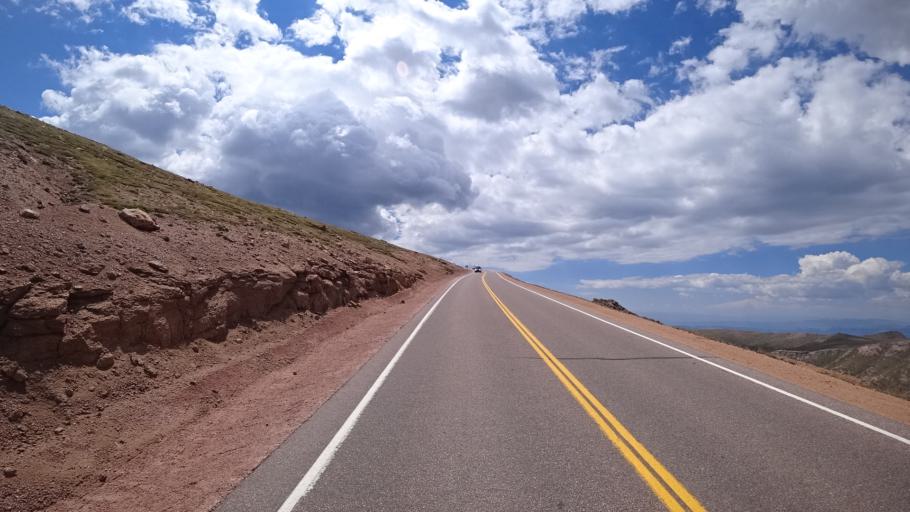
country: US
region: Colorado
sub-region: El Paso County
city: Cascade-Chipita Park
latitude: 38.8551
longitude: -105.0631
